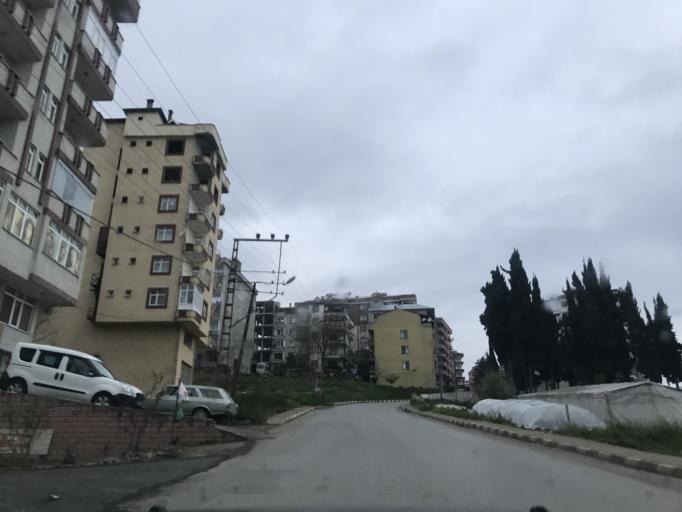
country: TR
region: Trabzon
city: Akcaabat
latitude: 41.0118
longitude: 39.5902
